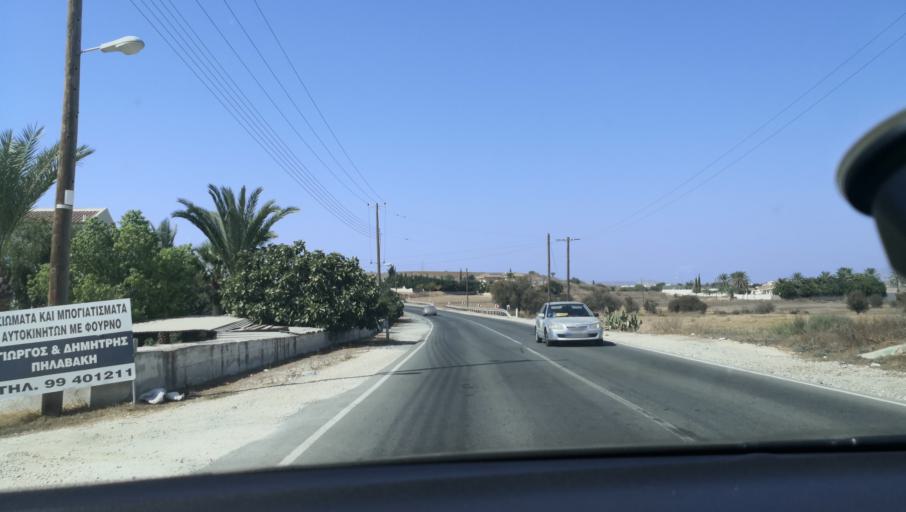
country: CY
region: Lefkosia
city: Kato Deftera
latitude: 35.1218
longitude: 33.2569
